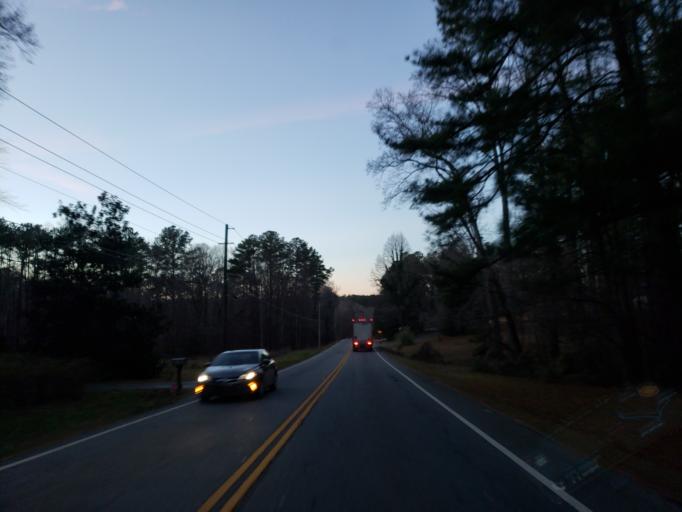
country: US
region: Georgia
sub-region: Paulding County
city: Hiram
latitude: 33.9546
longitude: -84.7051
